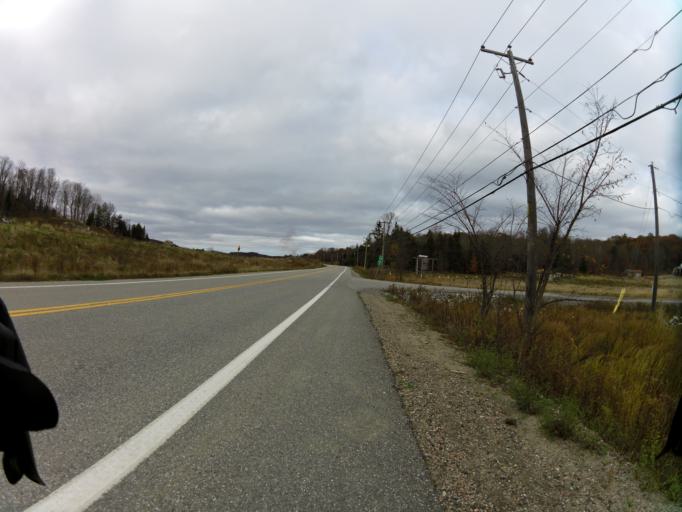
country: CA
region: Quebec
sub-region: Outaouais
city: Wakefield
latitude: 45.5863
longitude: -75.8883
